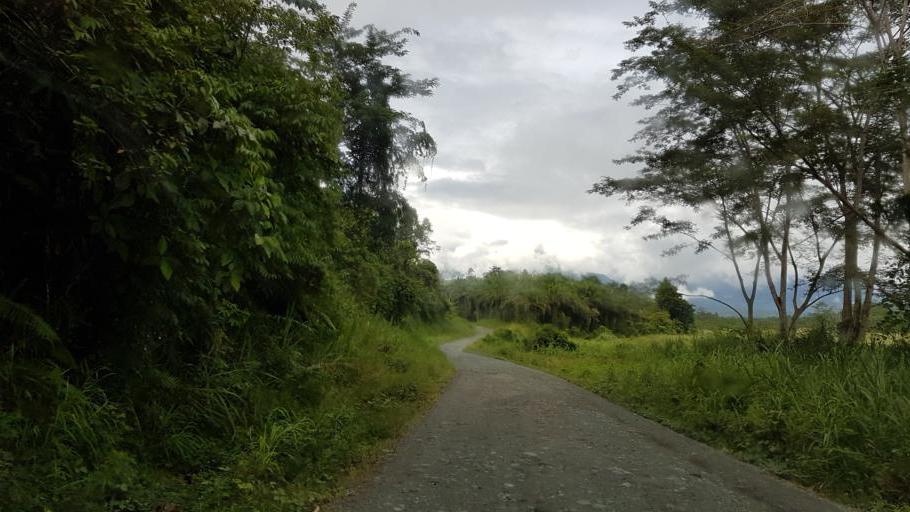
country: PG
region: Northern Province
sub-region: Sohe
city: Kokoda
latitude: -8.8819
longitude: 147.9911
